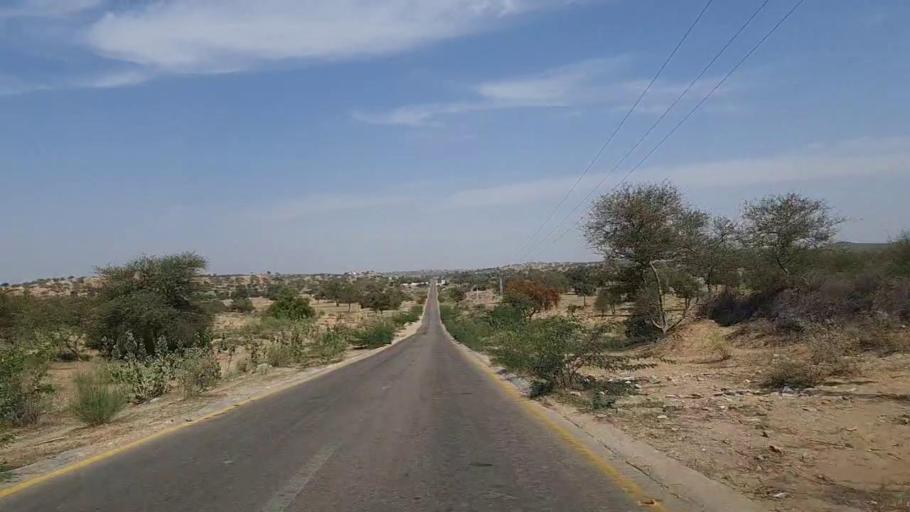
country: PK
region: Sindh
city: Mithi
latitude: 24.7827
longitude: 69.8109
